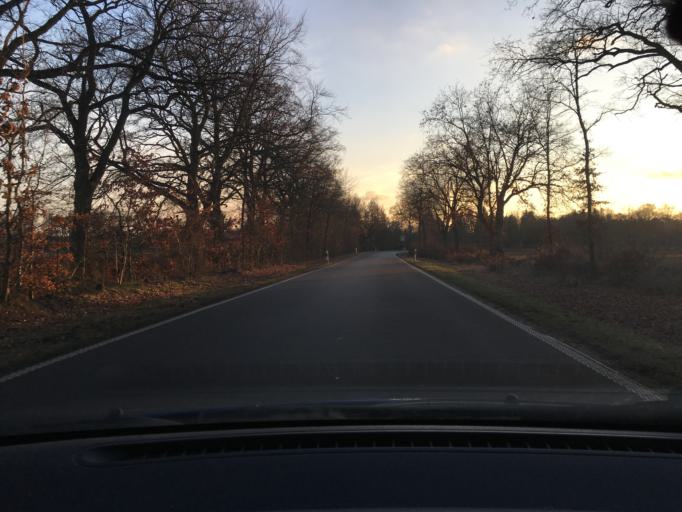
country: DE
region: Schleswig-Holstein
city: Langenlehsten
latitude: 53.4887
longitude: 10.7346
